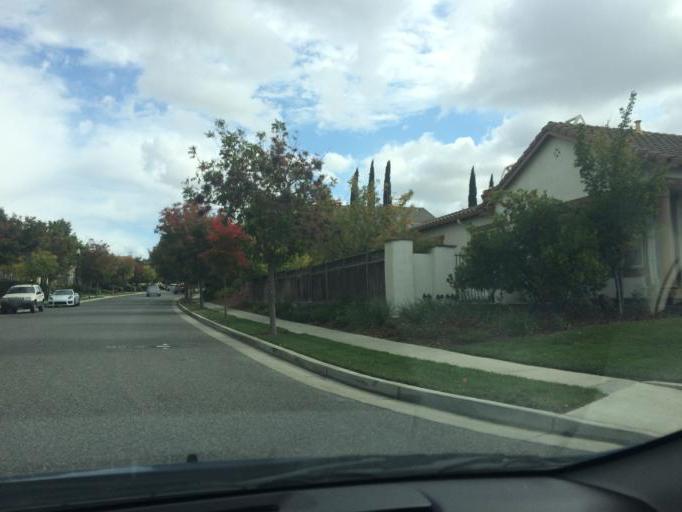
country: US
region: California
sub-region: Santa Clara County
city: Seven Trees
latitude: 37.2880
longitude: -121.7953
